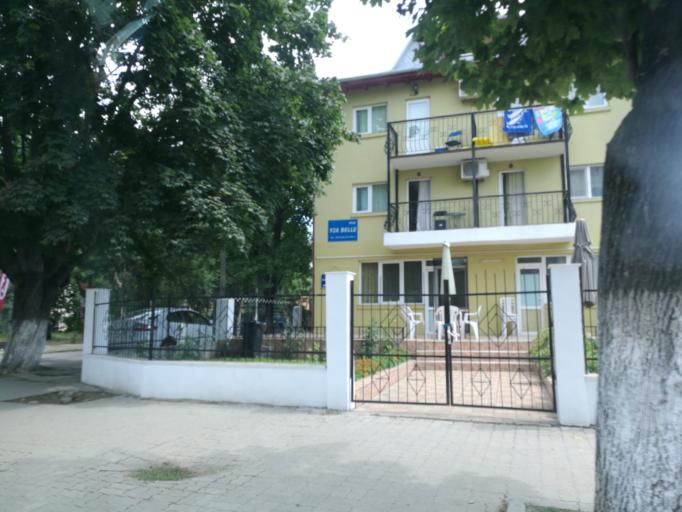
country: RO
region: Constanta
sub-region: Oras Eforie
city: Eforie Nord
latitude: 44.0666
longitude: 28.6334
